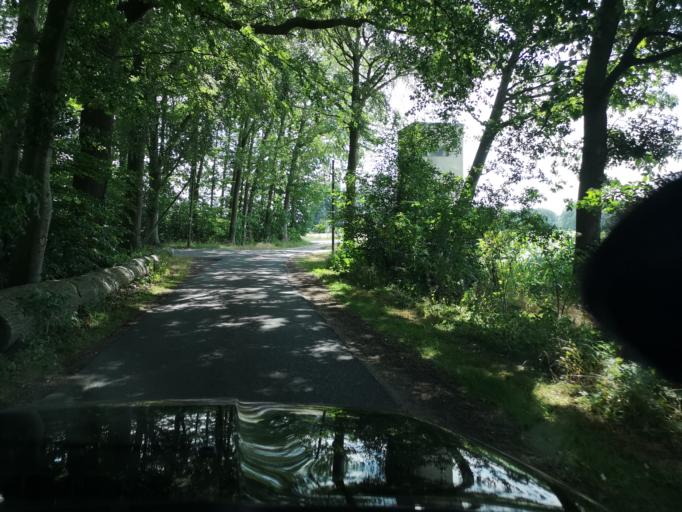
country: DE
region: North Rhine-Westphalia
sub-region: Regierungsbezirk Munster
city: Rhede
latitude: 51.8161
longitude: 6.6839
